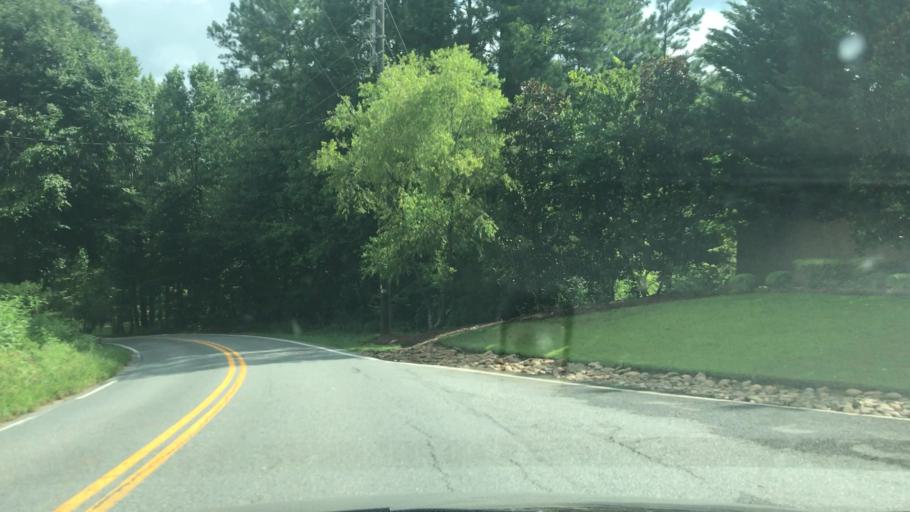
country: US
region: Georgia
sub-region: Fulton County
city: Johns Creek
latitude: 34.1231
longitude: -84.2008
